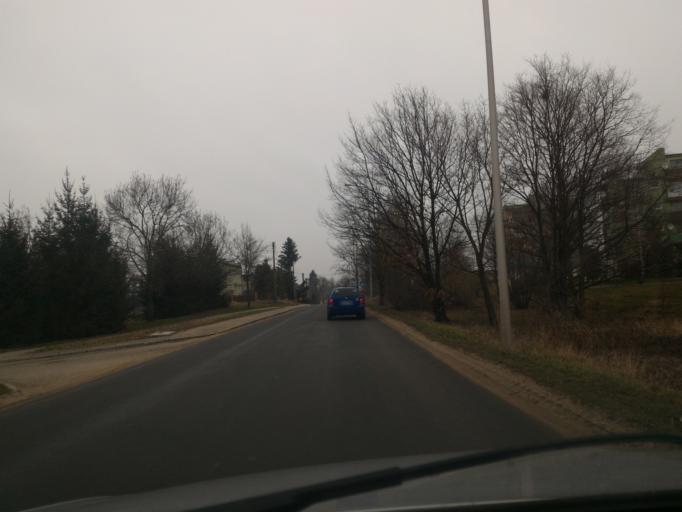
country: PL
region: Lower Silesian Voivodeship
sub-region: Powiat zgorzelecki
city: Bogatynia
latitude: 50.8997
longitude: 14.9537
